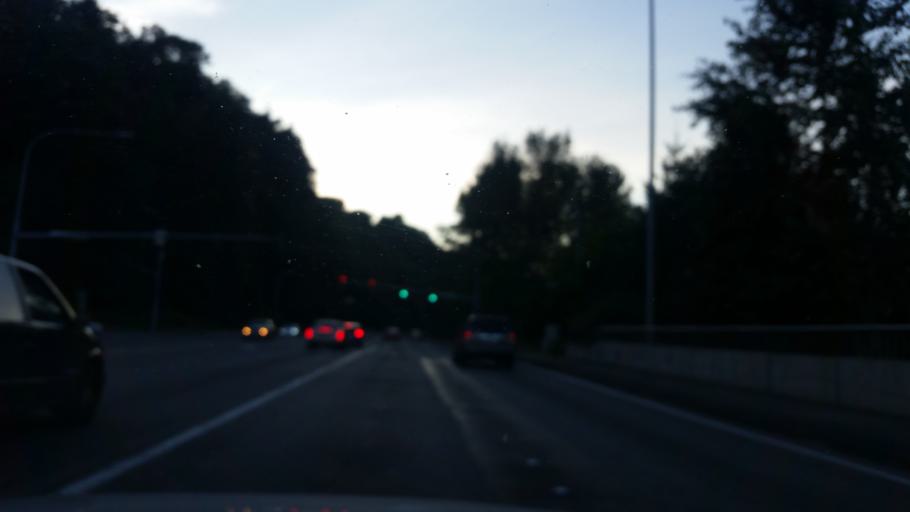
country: US
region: Washington
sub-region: King County
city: Tukwila
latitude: 47.4655
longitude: -122.2480
